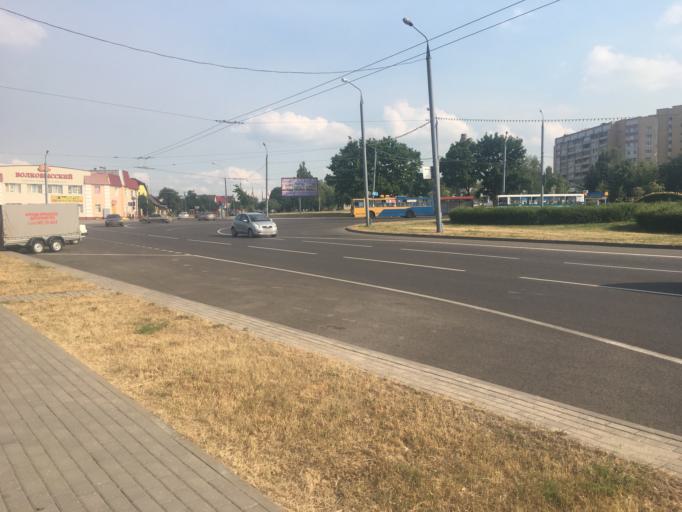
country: BY
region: Grodnenskaya
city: Hrodna
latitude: 53.6645
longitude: 23.8007
